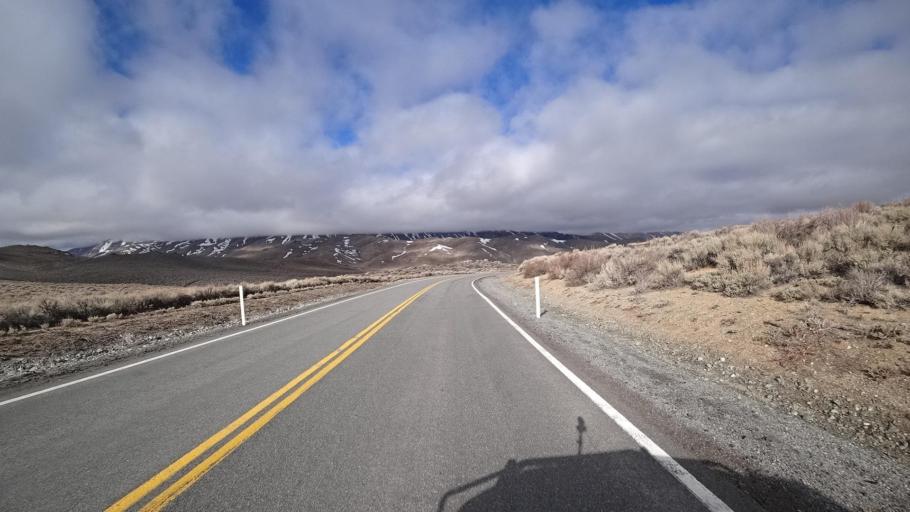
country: US
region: Nevada
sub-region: Washoe County
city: Cold Springs
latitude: 39.8023
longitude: -119.9115
